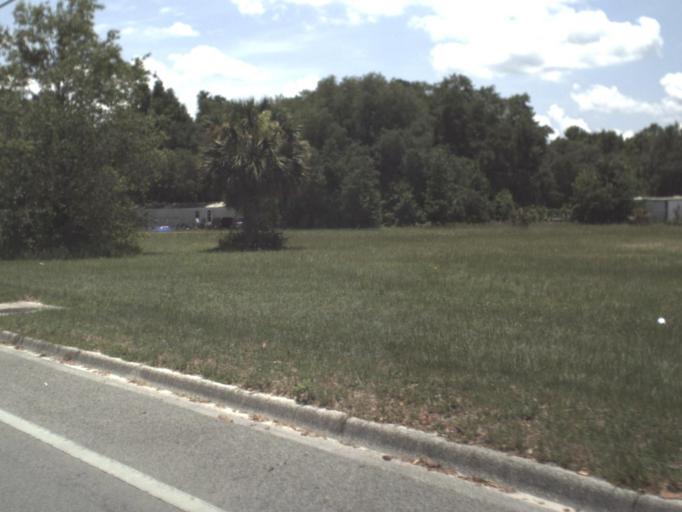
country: US
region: Florida
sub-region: Dixie County
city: Cross City
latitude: 29.6289
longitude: -83.1157
